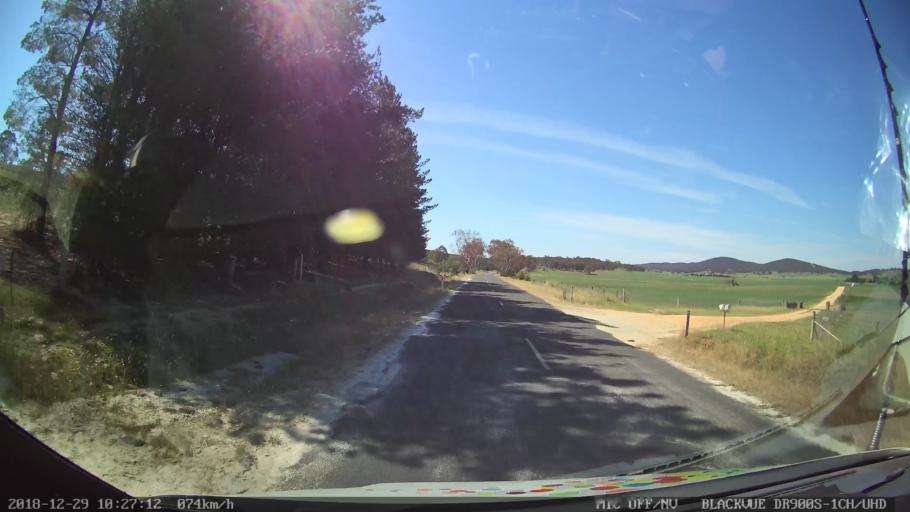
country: AU
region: New South Wales
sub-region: Yass Valley
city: Gundaroo
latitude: -34.9314
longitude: 149.4489
